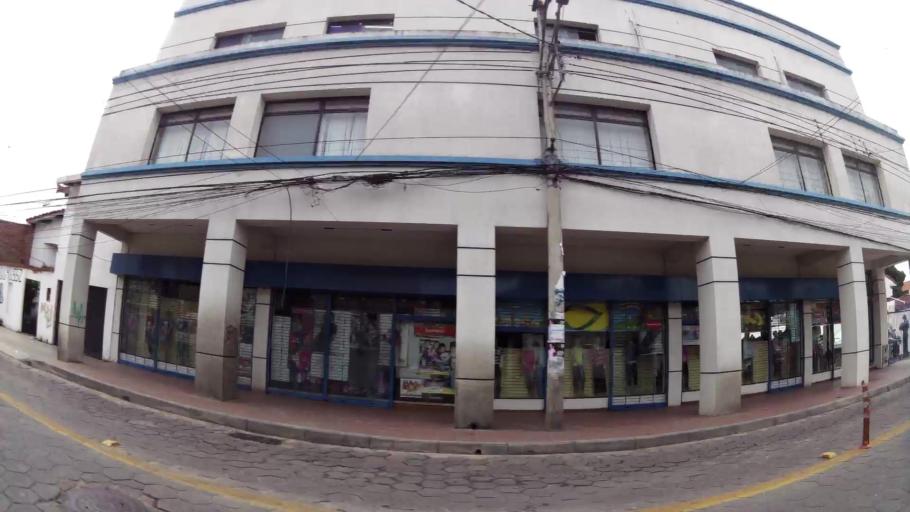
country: BO
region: Santa Cruz
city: Santa Cruz de la Sierra
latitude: -17.7888
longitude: -63.1784
